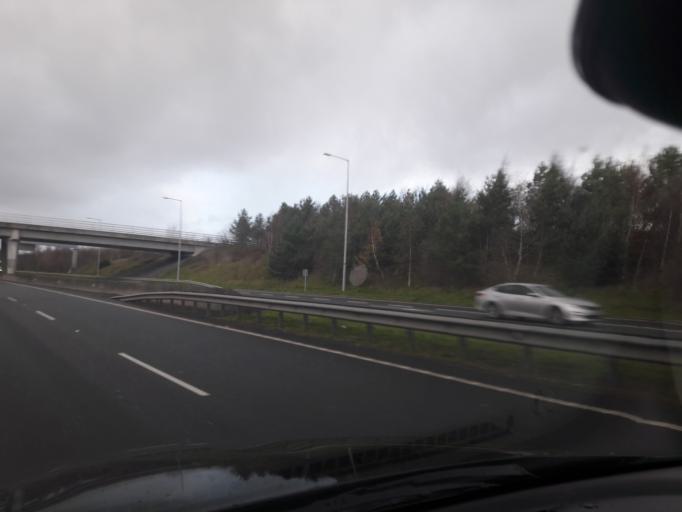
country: IE
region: Leinster
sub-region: An Mhi
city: Ashbourne
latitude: 53.4900
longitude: -6.3943
